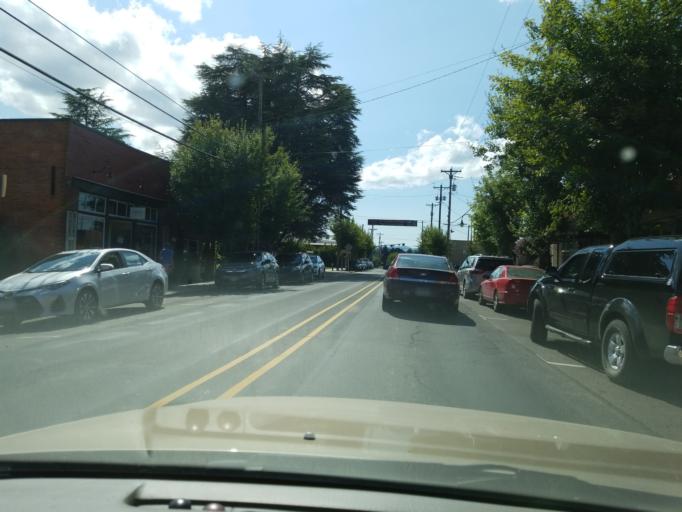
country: US
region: Oregon
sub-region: Yamhill County
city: Carlton
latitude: 45.2942
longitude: -123.1778
